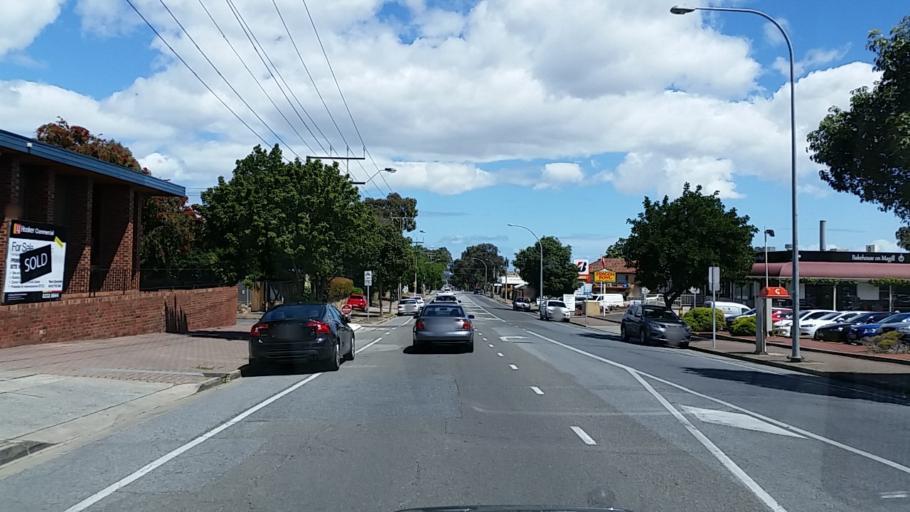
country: AU
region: South Australia
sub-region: Burnside
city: Wattle Park
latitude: -34.9131
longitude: 138.6742
